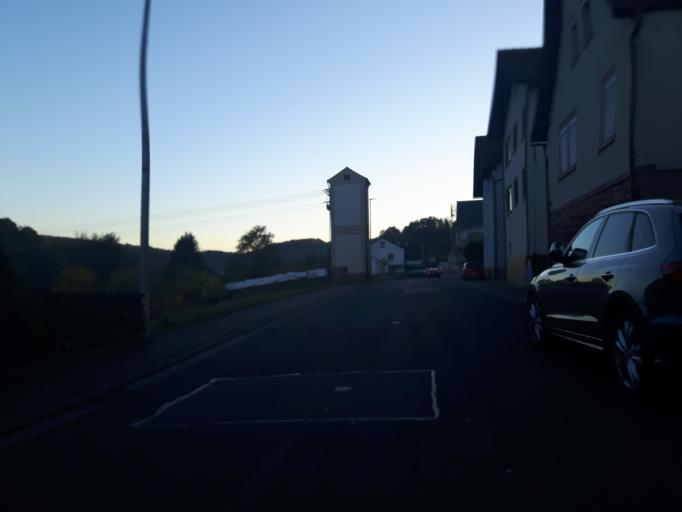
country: DE
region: Bavaria
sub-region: Regierungsbezirk Unterfranken
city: Heimbuchenthal
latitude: 49.8915
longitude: 9.2983
